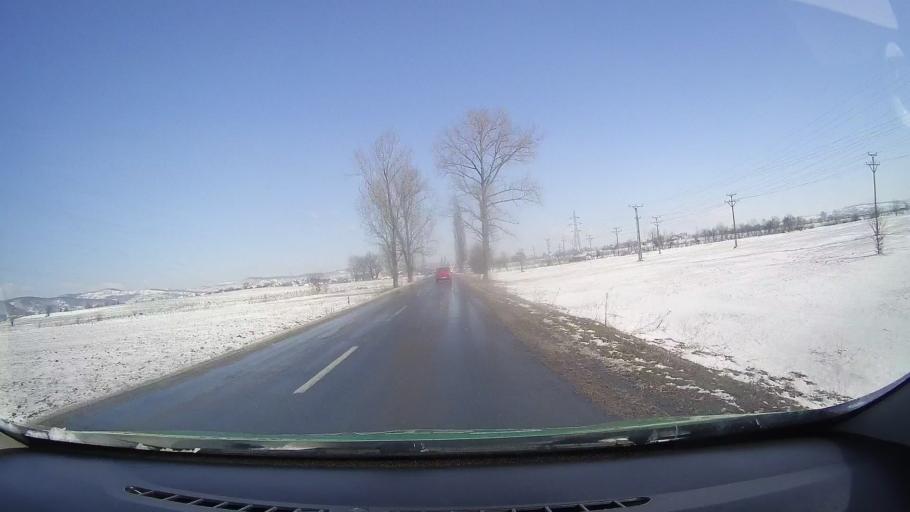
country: RO
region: Sibiu
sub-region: Comuna Avrig
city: Avrig
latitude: 45.7139
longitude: 24.3709
